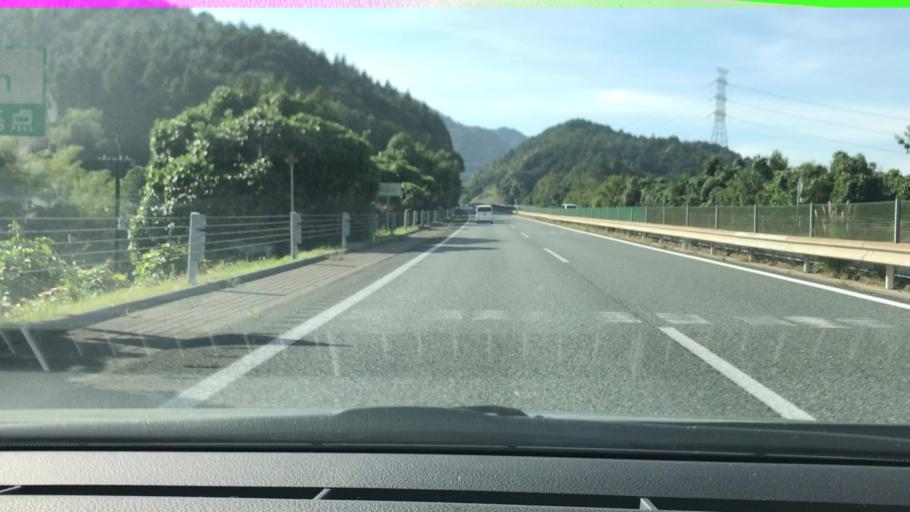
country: JP
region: Hyogo
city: Sasayama
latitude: 35.0457
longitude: 135.1824
